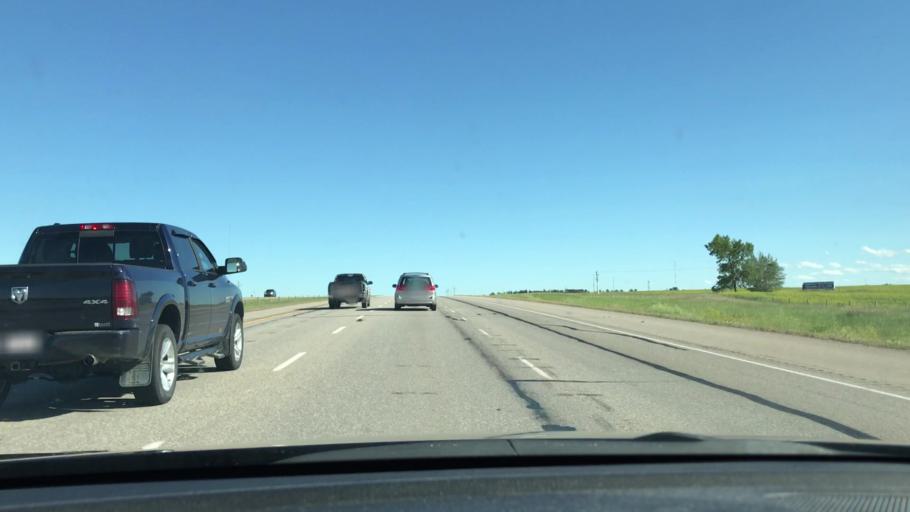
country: CA
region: Alberta
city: Crossfield
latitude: 51.4486
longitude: -114.0137
